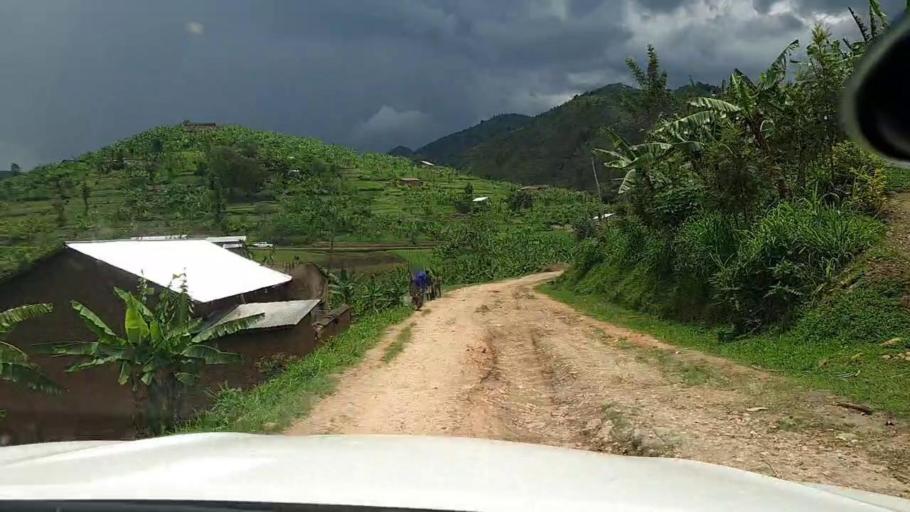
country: RW
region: Western Province
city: Kibuye
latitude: -2.0730
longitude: 29.4348
